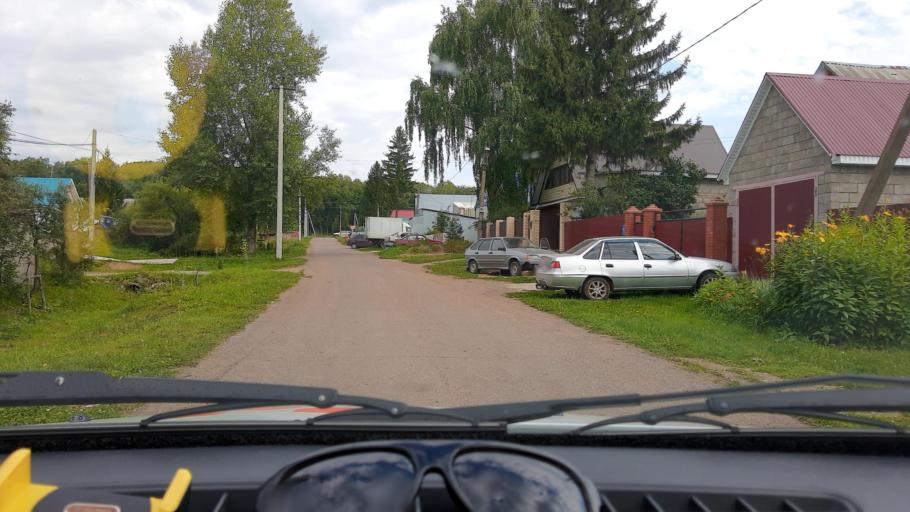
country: RU
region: Bashkortostan
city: Mikhaylovka
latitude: 54.8178
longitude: 55.8004
